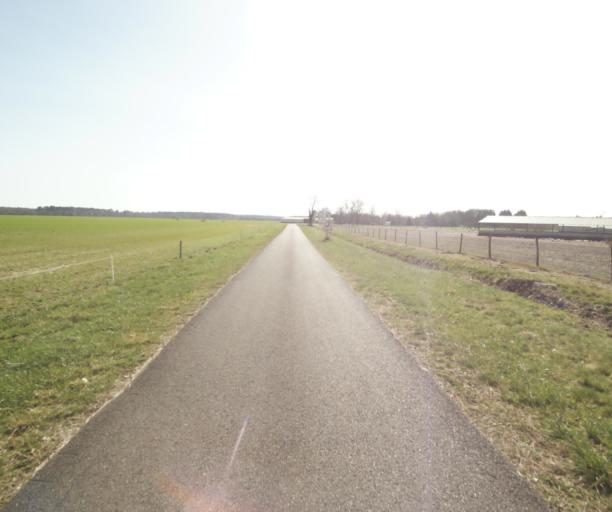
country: FR
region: Aquitaine
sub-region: Departement des Landes
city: Roquefort
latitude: 44.1568
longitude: -0.2496
